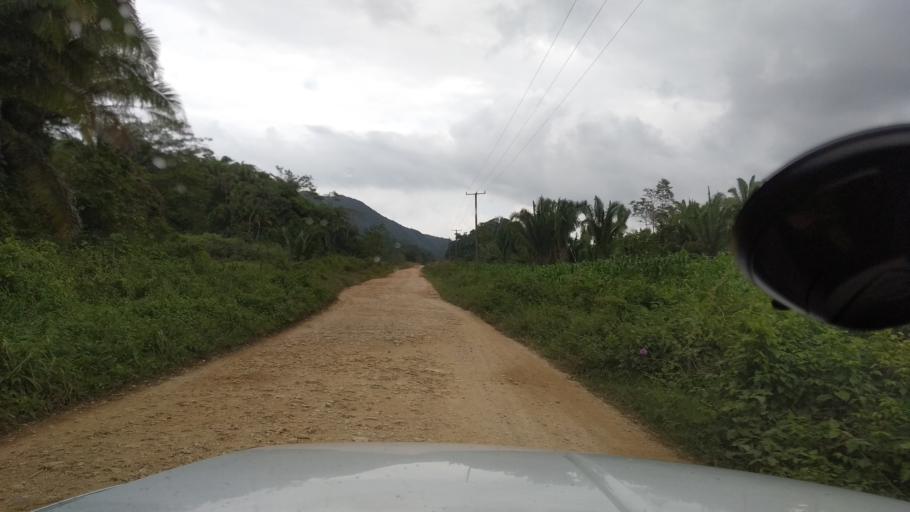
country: BZ
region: Toledo
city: Punta Gorda
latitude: 16.2028
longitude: -89.0343
